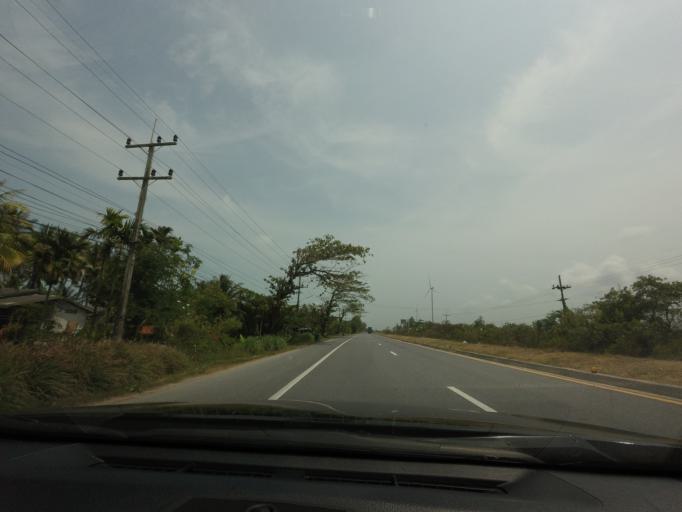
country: TH
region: Nakhon Si Thammarat
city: Hua Sai
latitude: 7.9640
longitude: 100.3292
